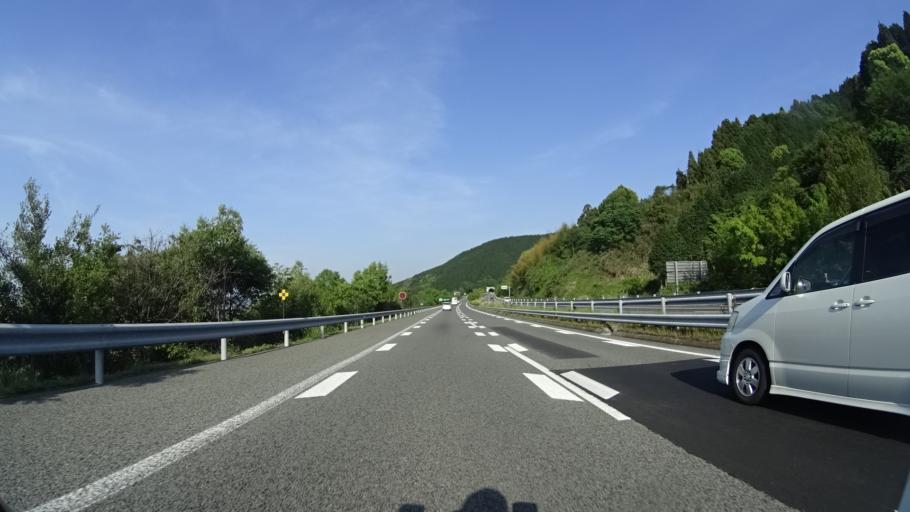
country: JP
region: Ehime
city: Saijo
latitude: 33.8859
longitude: 133.1395
